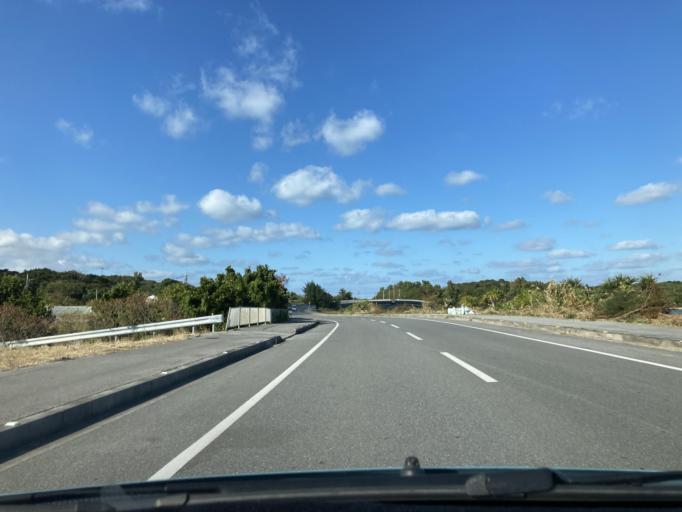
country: JP
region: Okinawa
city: Katsuren-haebaru
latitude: 26.3135
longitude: 127.9190
